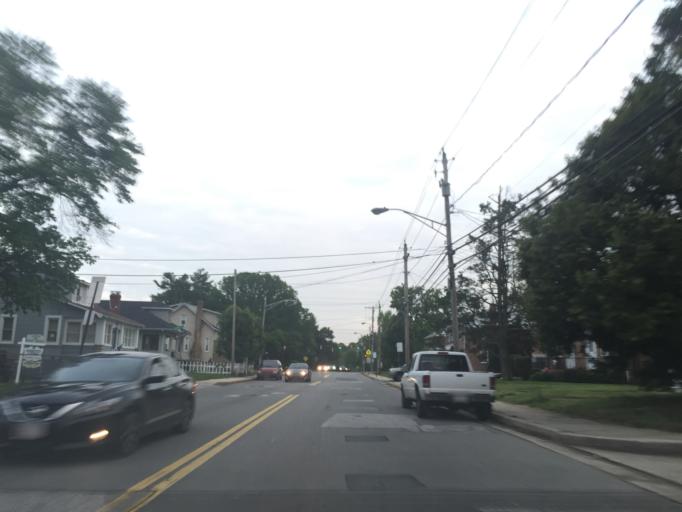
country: US
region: Maryland
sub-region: Baltimore County
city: Parkville
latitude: 39.3704
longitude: -76.5388
